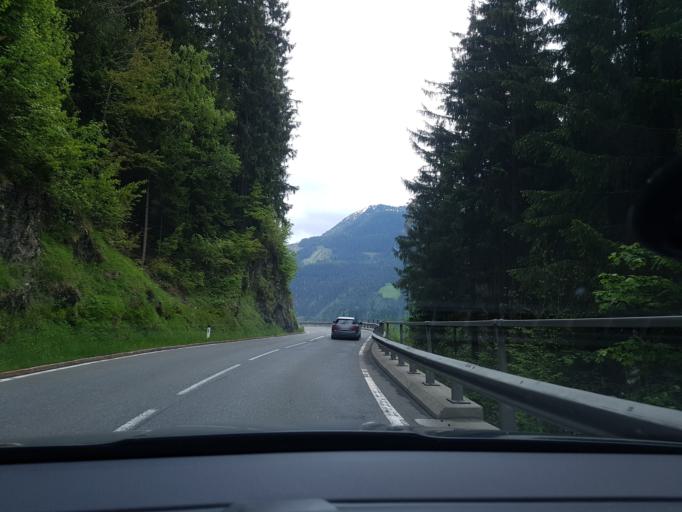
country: AT
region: Salzburg
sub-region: Politischer Bezirk Zell am See
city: Mittersill
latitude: 47.2915
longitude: 12.4467
